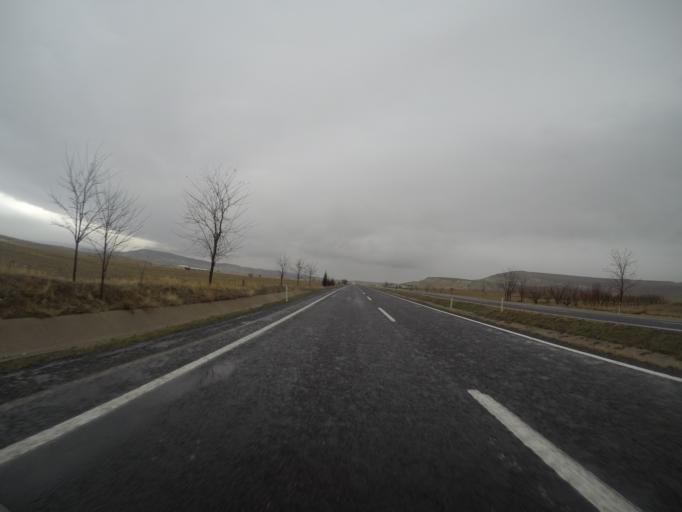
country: TR
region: Nevsehir
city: Urgub
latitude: 38.7302
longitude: 34.9659
